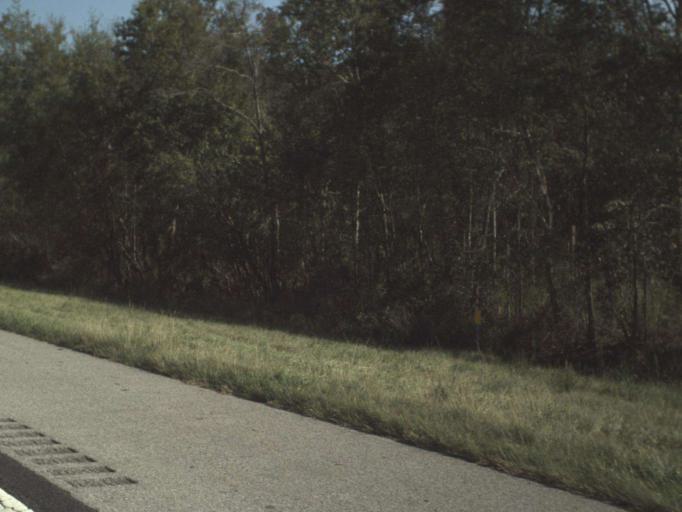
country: US
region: Florida
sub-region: Washington County
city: Chipley
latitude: 30.7512
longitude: -85.5760
